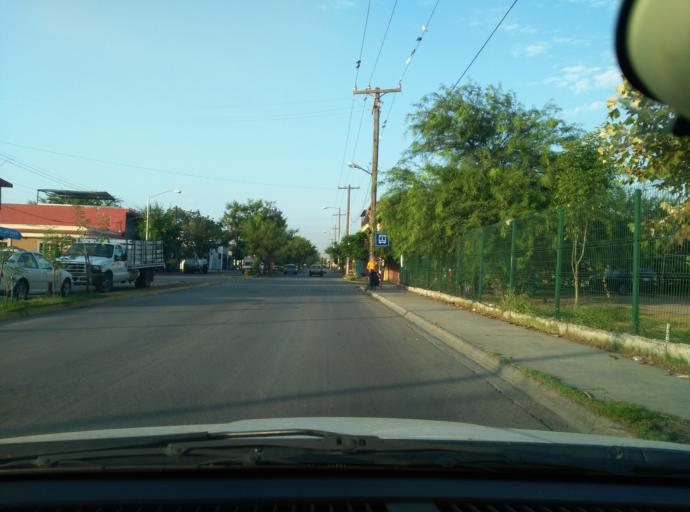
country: MX
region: Nuevo Leon
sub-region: Apodaca
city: Fraccionamiento Cosmopolis Octavo Sector
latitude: 25.7667
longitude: -100.2490
